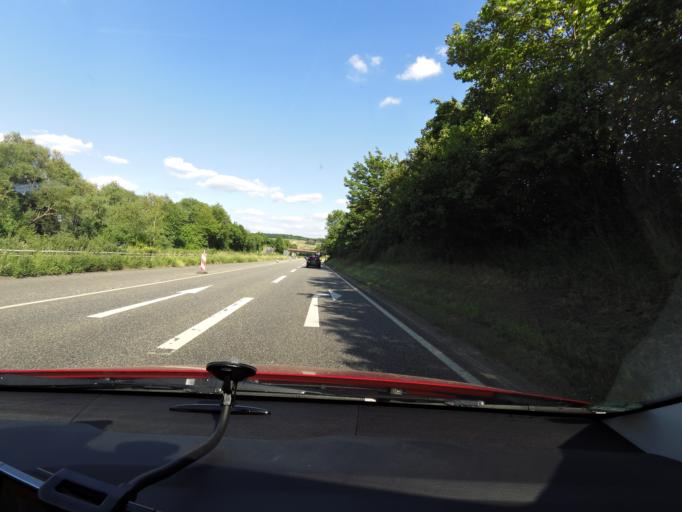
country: DE
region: Rheinland-Pfalz
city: Konigsfeld
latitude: 50.5466
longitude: 7.1785
